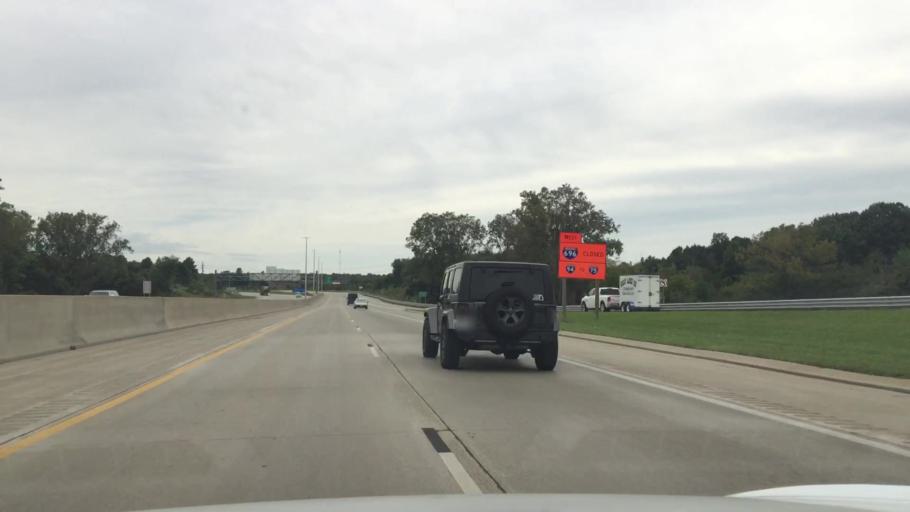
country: US
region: Michigan
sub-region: Saint Clair County
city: Port Huron
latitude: 42.9896
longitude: -82.4604
